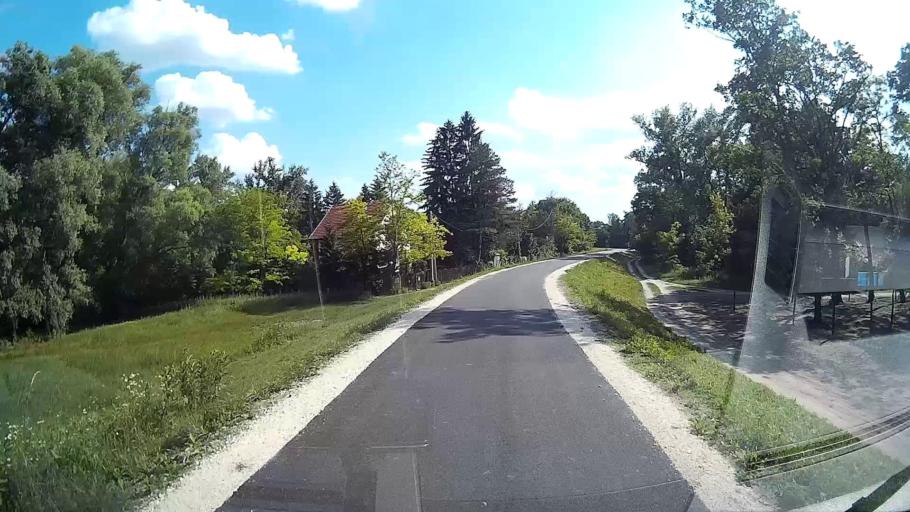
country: HU
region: Pest
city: God
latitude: 47.6669
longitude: 19.1122
